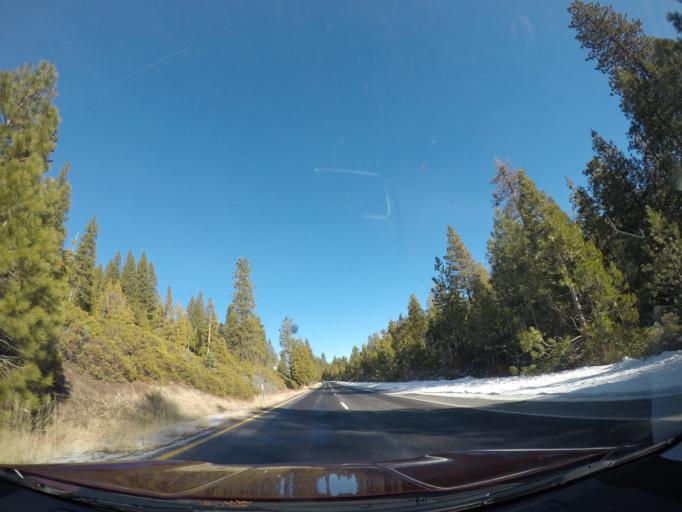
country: US
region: California
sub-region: Tuolumne County
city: Twain Harte
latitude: 38.1241
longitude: -120.1103
